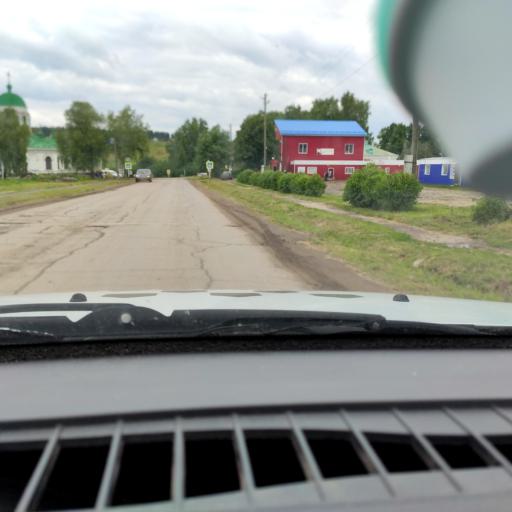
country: RU
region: Perm
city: Uinskoye
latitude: 57.1168
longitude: 56.5255
